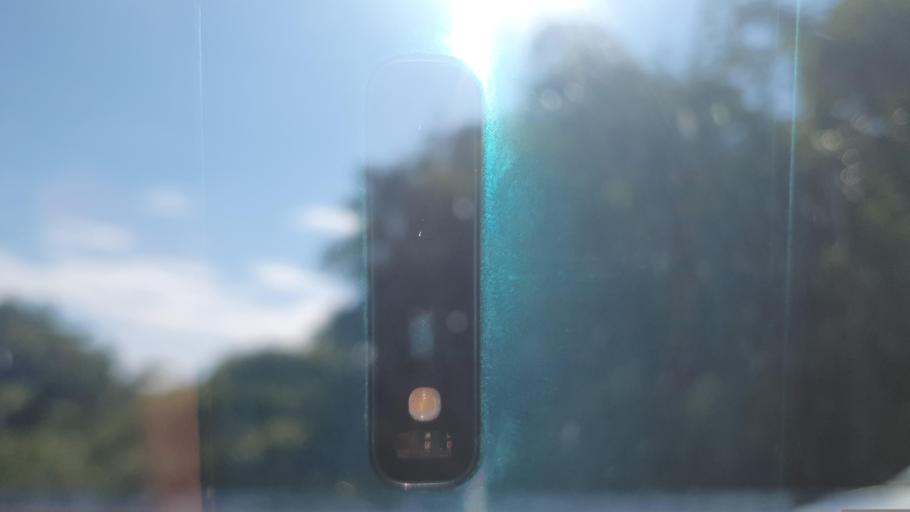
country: TW
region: Taiwan
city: Yujing
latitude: 23.0558
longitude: 120.4015
